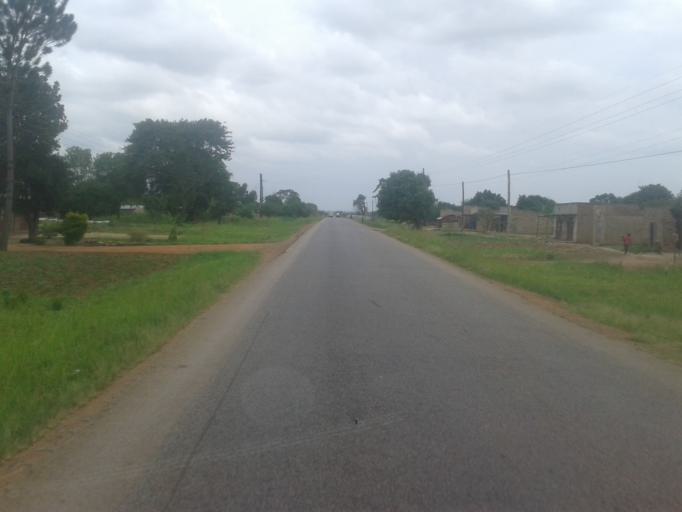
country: UG
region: Western Region
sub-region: Kiryandongo District
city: Masindi Port
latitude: 1.5159
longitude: 32.0668
